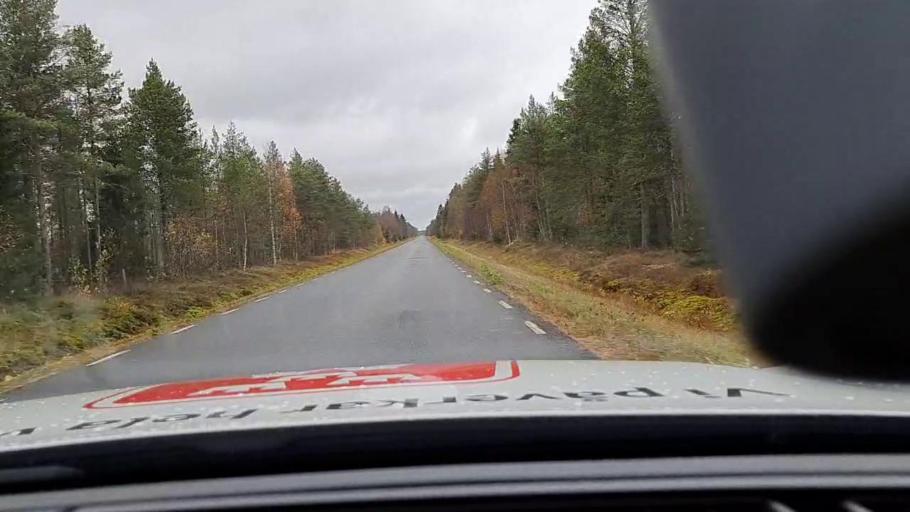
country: SE
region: Norrbotten
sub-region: Haparanda Kommun
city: Haparanda
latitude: 65.9111
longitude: 23.8293
